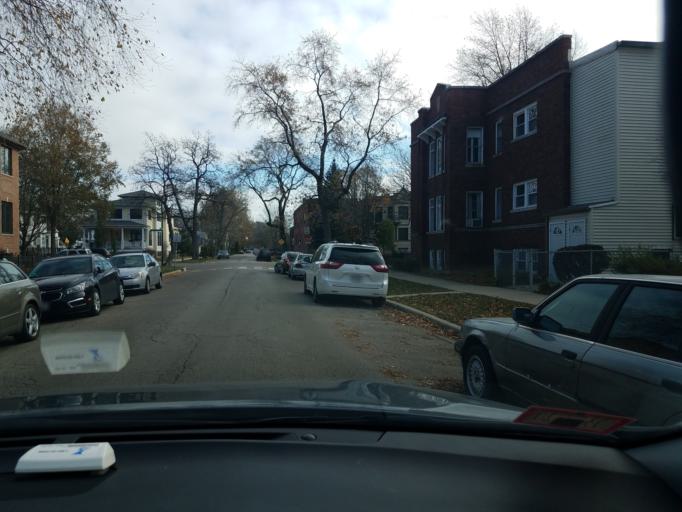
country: US
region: Illinois
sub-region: Cook County
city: Lincolnwood
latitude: 41.9481
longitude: -87.7330
